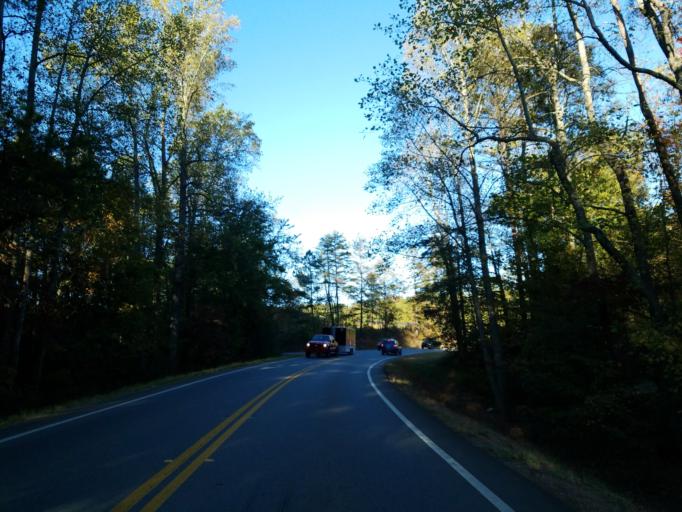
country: US
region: Georgia
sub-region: Dawson County
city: Dawsonville
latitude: 34.4303
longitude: -84.1774
